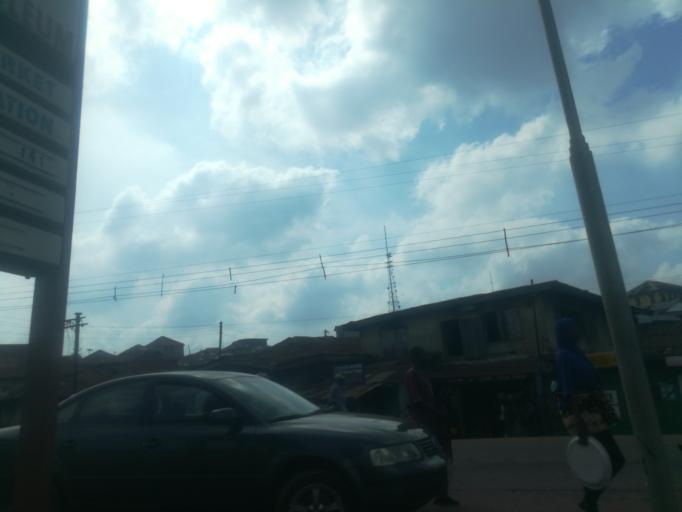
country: NG
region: Oyo
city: Ibadan
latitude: 7.3788
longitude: 3.8961
